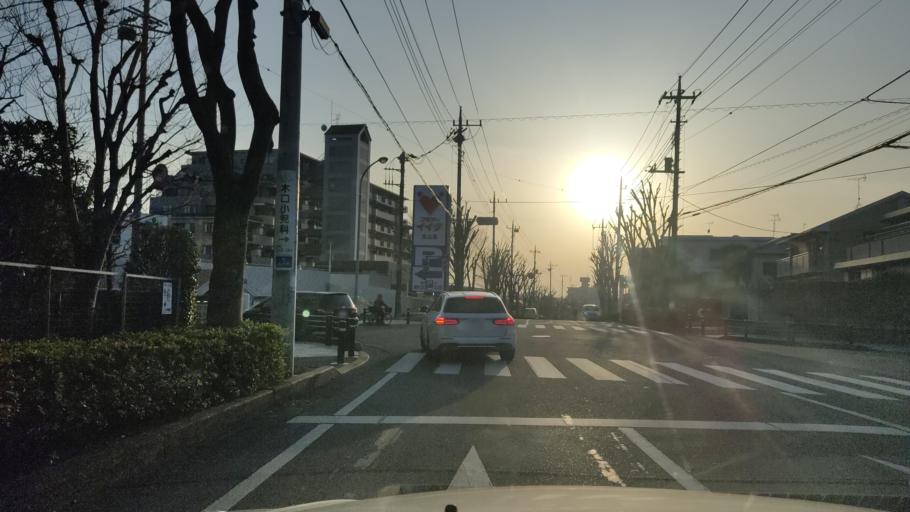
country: JP
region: Chiba
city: Nagareyama
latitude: 35.8618
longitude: 139.9072
